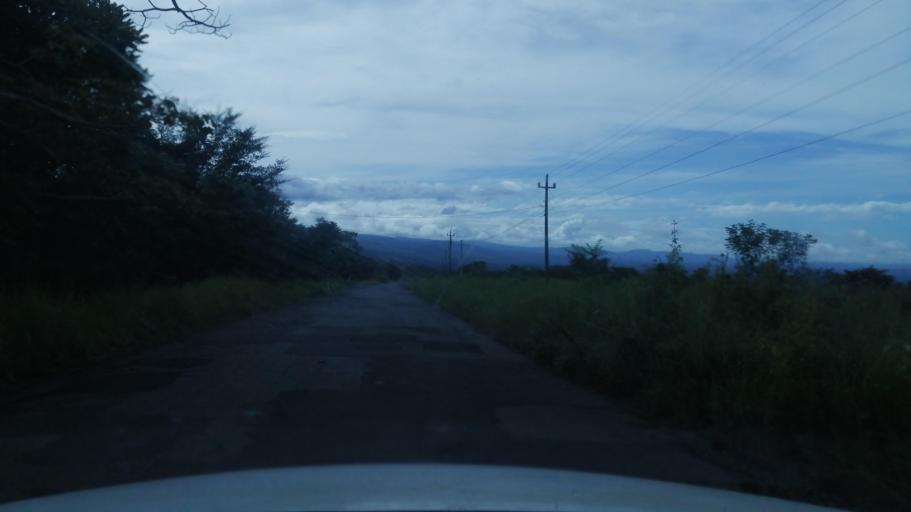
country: PA
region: Chiriqui
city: Potrerillos Abajo
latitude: 8.6713
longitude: -82.4359
